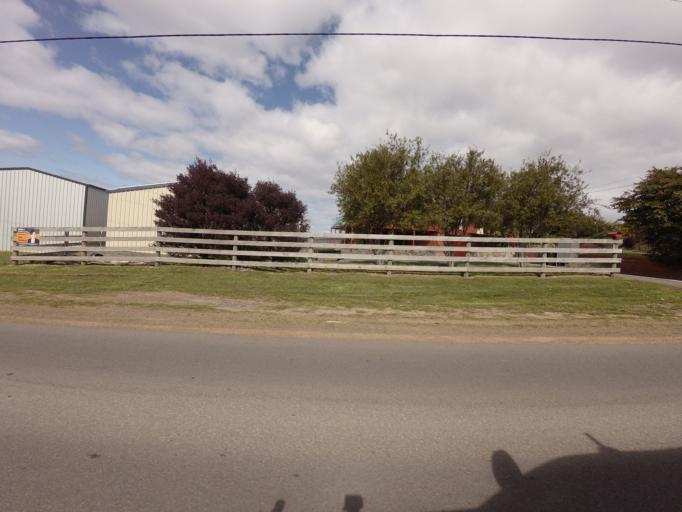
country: AU
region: Tasmania
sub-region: Huon Valley
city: Geeveston
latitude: -43.3207
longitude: 147.0068
